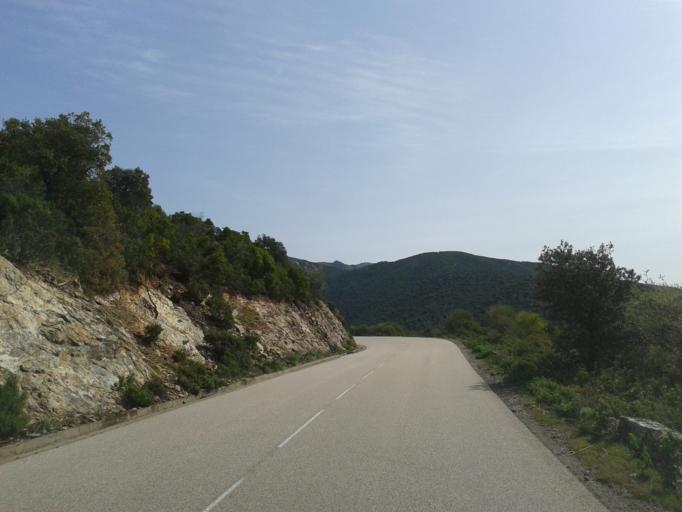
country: FR
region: Corsica
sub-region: Departement de la Haute-Corse
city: Monticello
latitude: 42.6528
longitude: 9.1116
